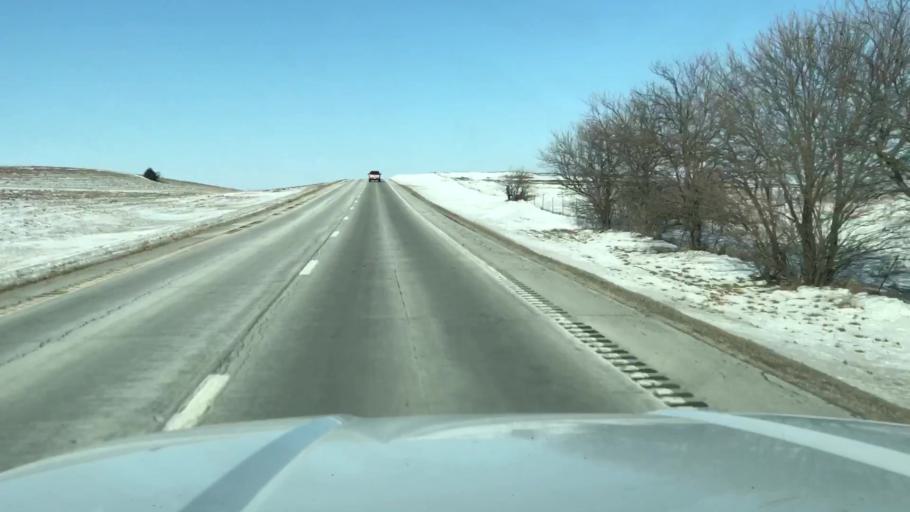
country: US
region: Missouri
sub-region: Andrew County
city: Savannah
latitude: 39.9710
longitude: -94.8717
